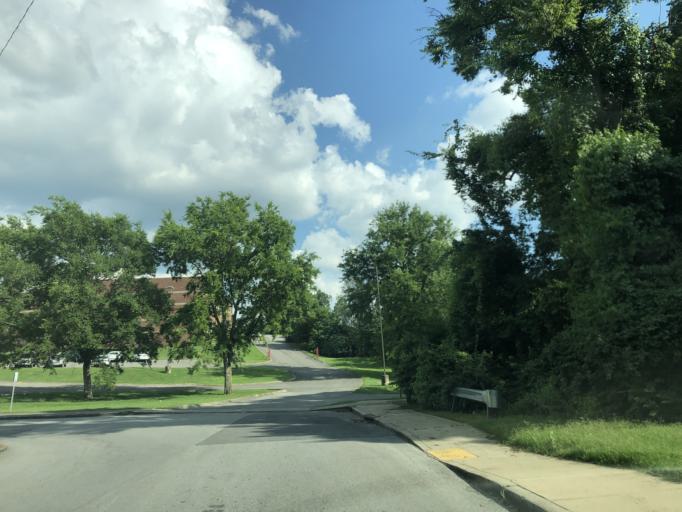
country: US
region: Tennessee
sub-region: Davidson County
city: Nashville
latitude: 36.1614
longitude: -86.8331
